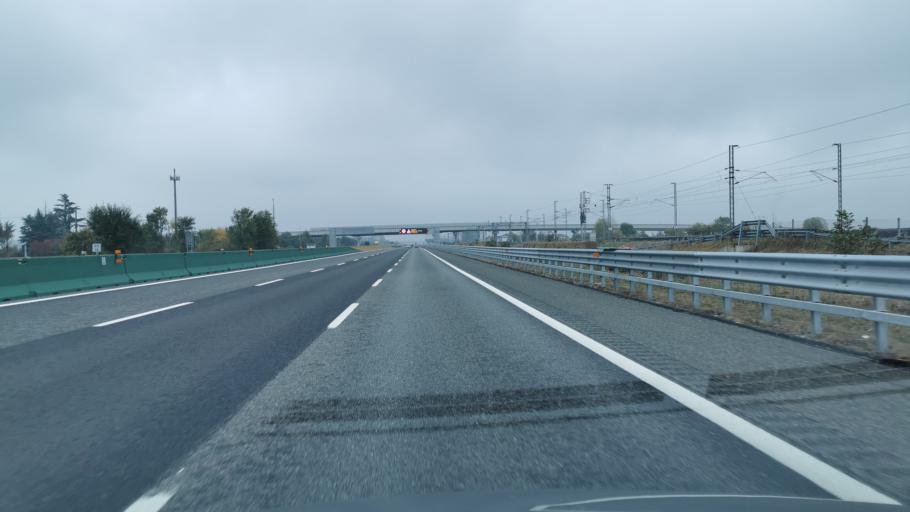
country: IT
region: Piedmont
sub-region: Provincia di Vercelli
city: Cigliano
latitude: 45.2925
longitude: 8.0416
